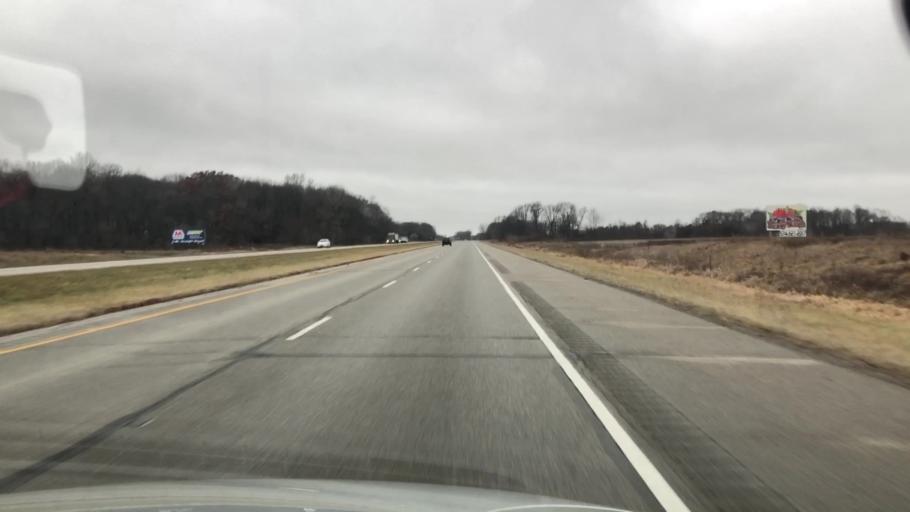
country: US
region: Indiana
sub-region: Kosciusko County
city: Mentone
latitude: 41.2686
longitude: -86.0023
